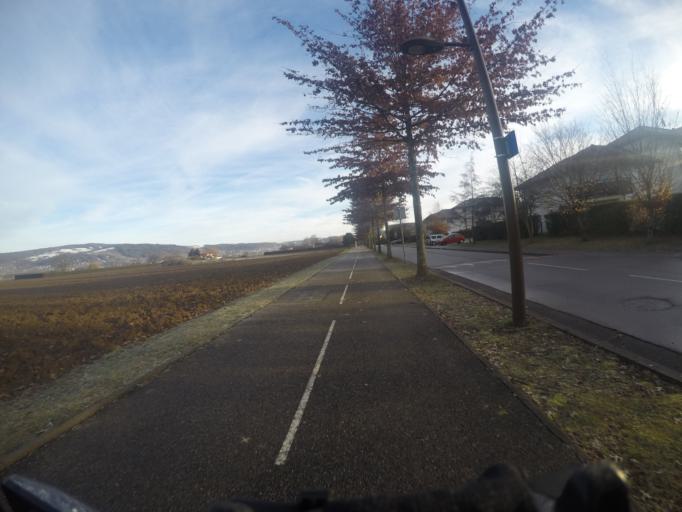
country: FR
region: Rhone-Alpes
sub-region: Departement de la Haute-Savoie
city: Meythet
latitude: 45.9218
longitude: 6.0956
